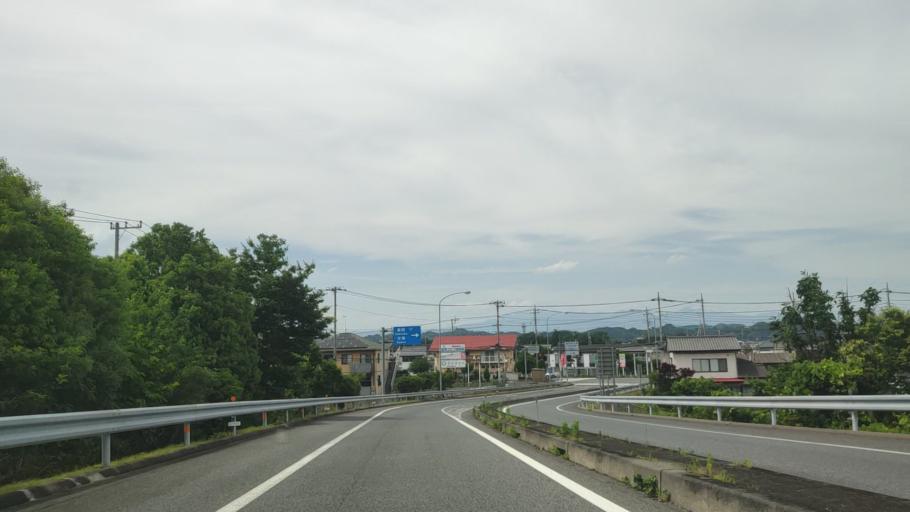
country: JP
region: Gunma
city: Tomioka
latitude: 36.2446
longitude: 138.8940
